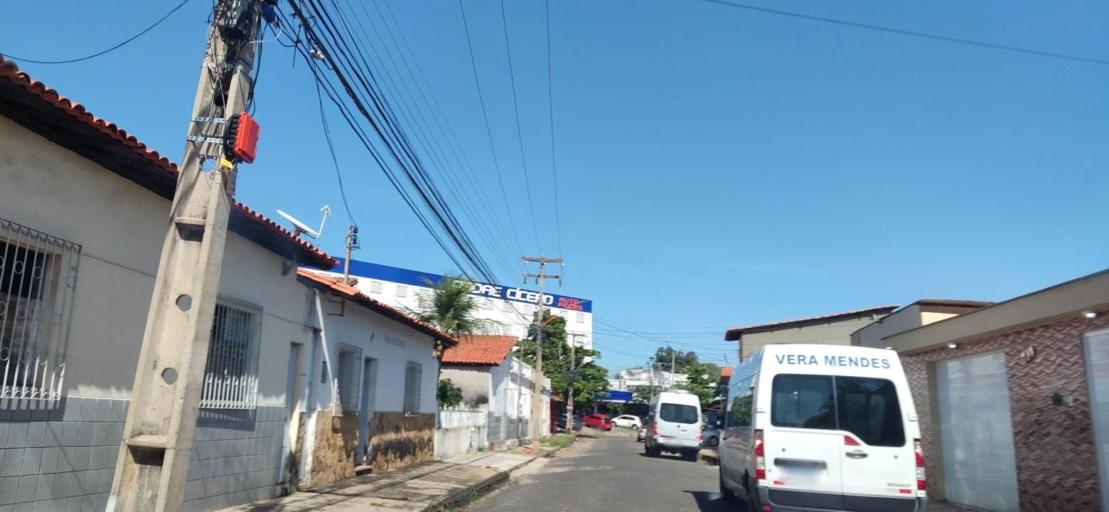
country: BR
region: Piaui
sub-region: Teresina
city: Teresina
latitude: -5.0984
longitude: -42.8017
